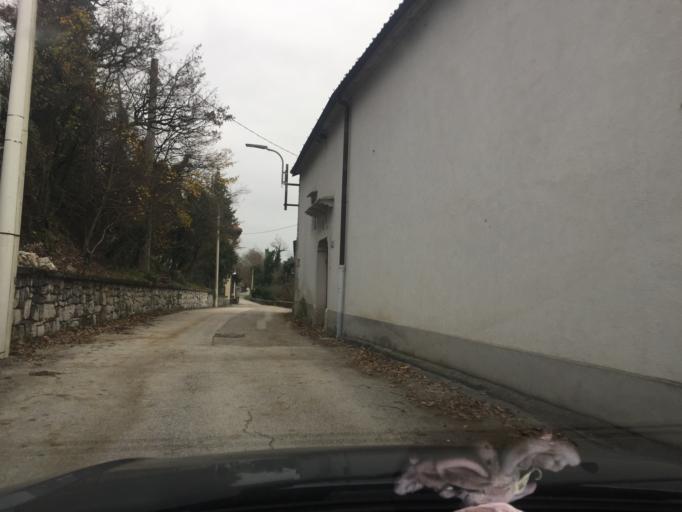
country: IT
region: Friuli Venezia Giulia
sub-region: Provincia di Trieste
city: Zolla
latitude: 45.7195
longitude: 13.8037
